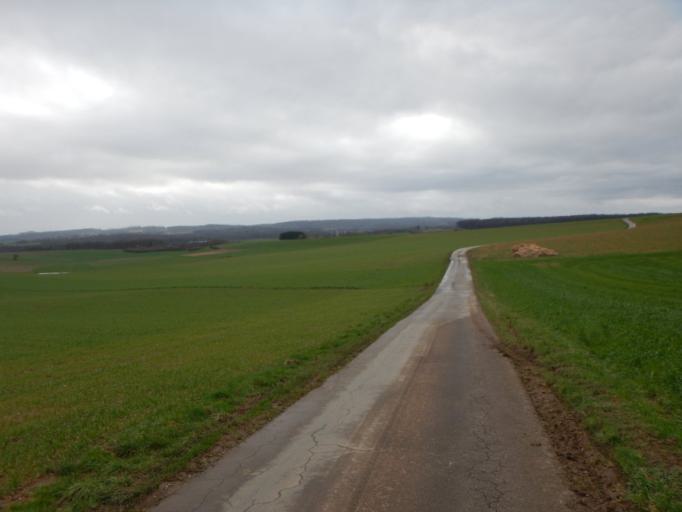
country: BE
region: Wallonia
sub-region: Province du Luxembourg
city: Attert
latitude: 49.7755
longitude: 5.8025
